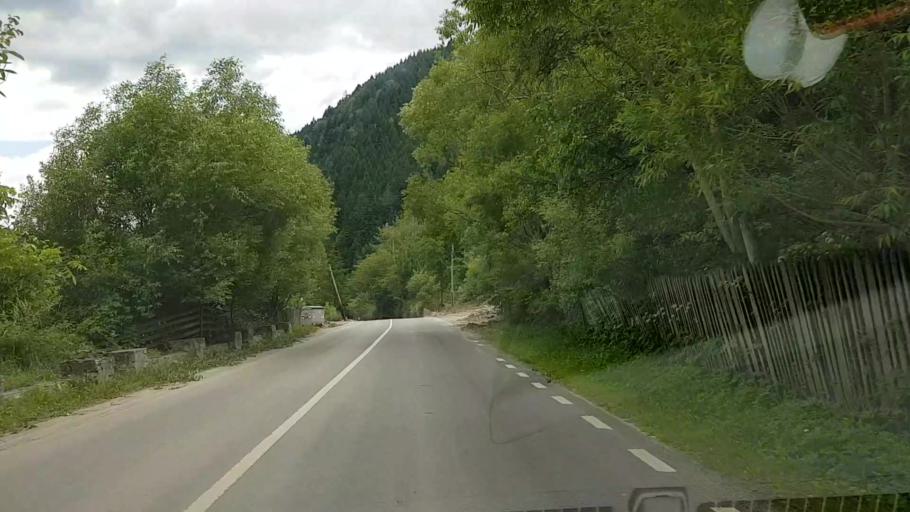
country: RO
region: Neamt
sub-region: Comuna Poiana Teiului
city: Poiana Teiului
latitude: 47.0954
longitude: 25.9434
